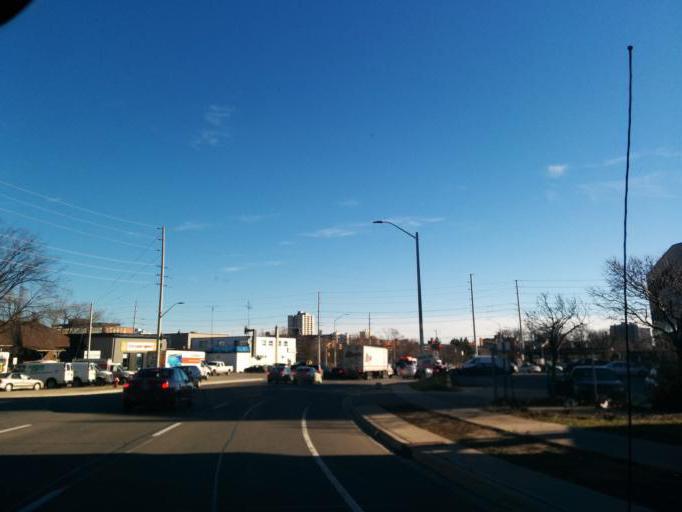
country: CA
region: Ontario
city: Mississauga
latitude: 43.5782
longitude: -79.6211
